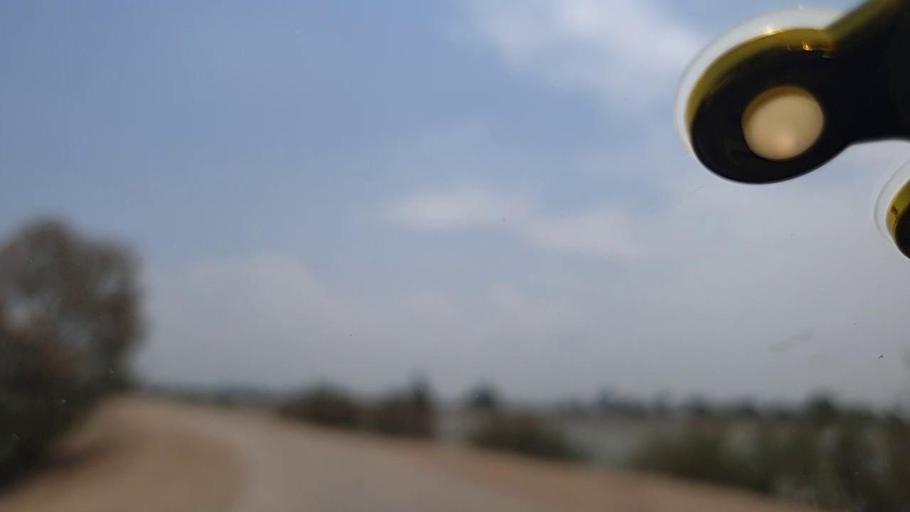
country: PK
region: Sindh
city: Rustam jo Goth
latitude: 28.1082
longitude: 68.8896
